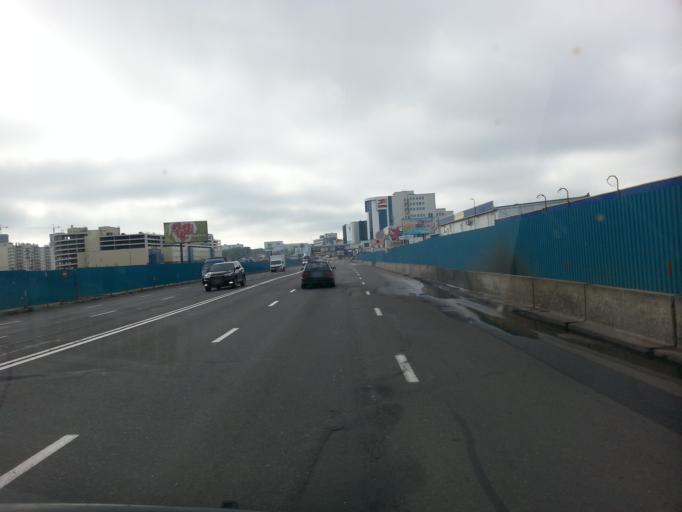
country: BY
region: Minsk
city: Zhdanovichy
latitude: 53.9355
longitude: 27.4521
